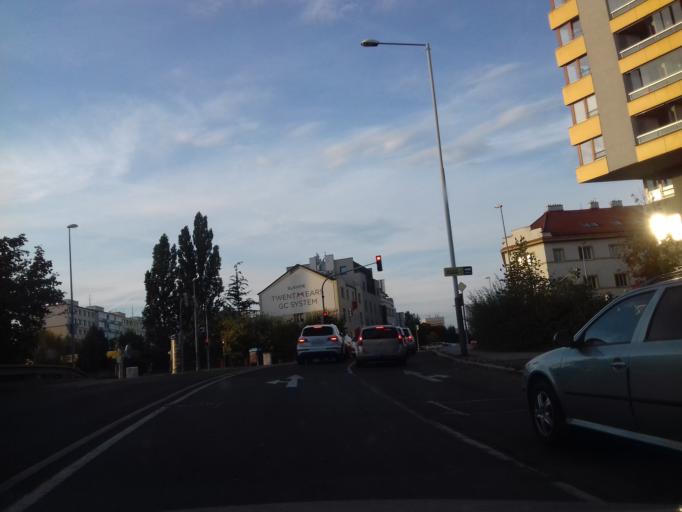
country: CZ
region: Praha
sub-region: Praha 4
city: Hodkovicky
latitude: 50.0399
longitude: 14.4384
